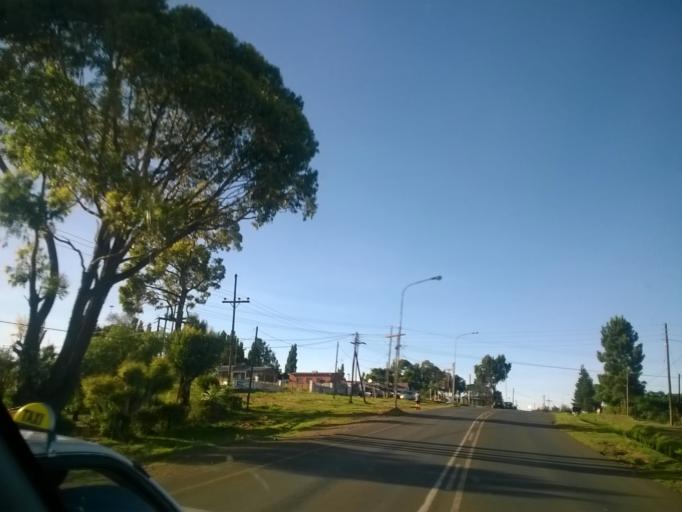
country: LS
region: Maseru
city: Maseru
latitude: -29.2824
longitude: 27.5280
